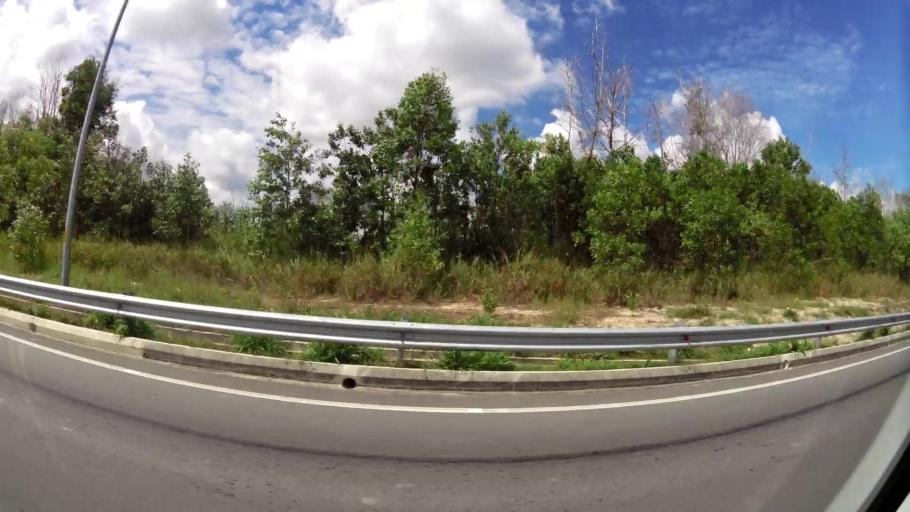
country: BN
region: Brunei and Muara
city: Bandar Seri Begawan
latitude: 4.9324
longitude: 114.8877
